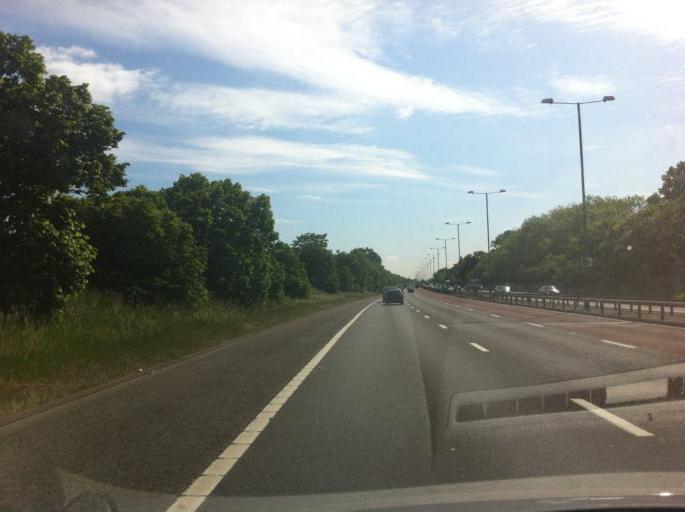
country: GB
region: England
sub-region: Greater London
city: Southall
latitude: 51.4938
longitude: -0.3571
